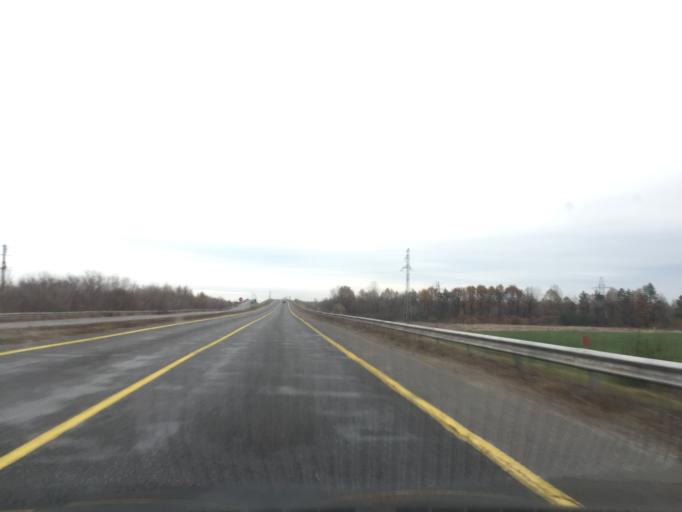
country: BY
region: Gomel
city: Horad Rechytsa
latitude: 52.3181
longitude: 30.5179
